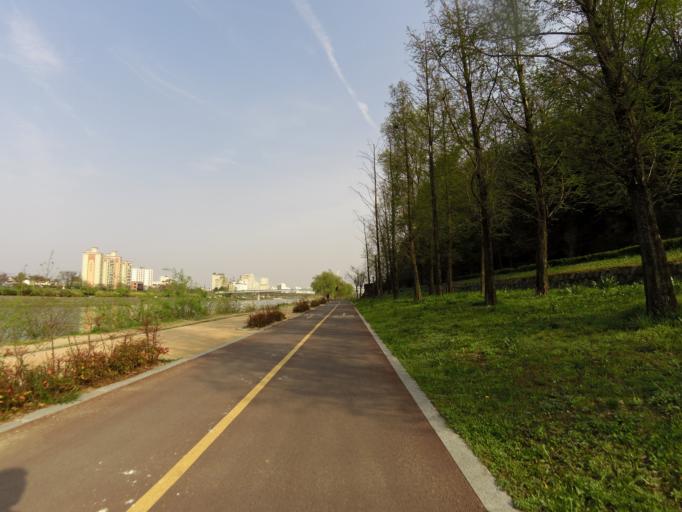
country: KR
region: Daegu
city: Daegu
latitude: 35.8867
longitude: 128.6441
